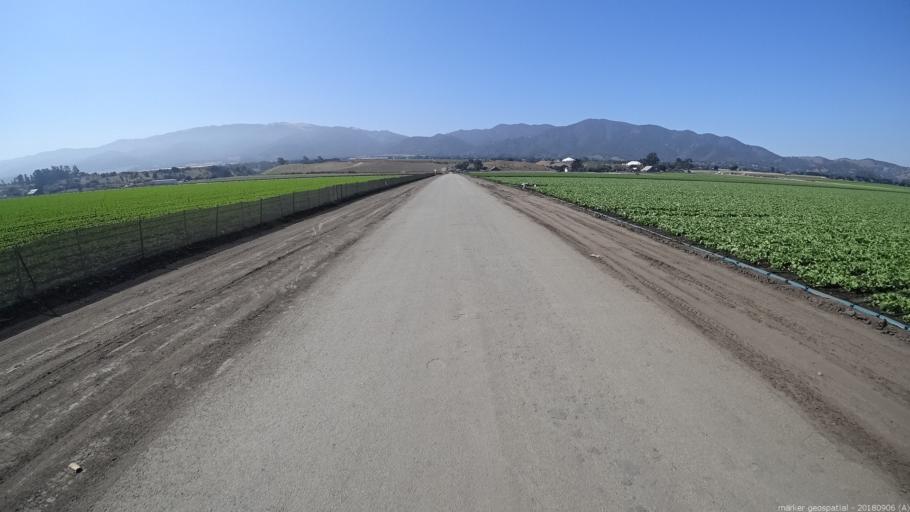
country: US
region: California
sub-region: Monterey County
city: Salinas
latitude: 36.5997
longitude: -121.6171
